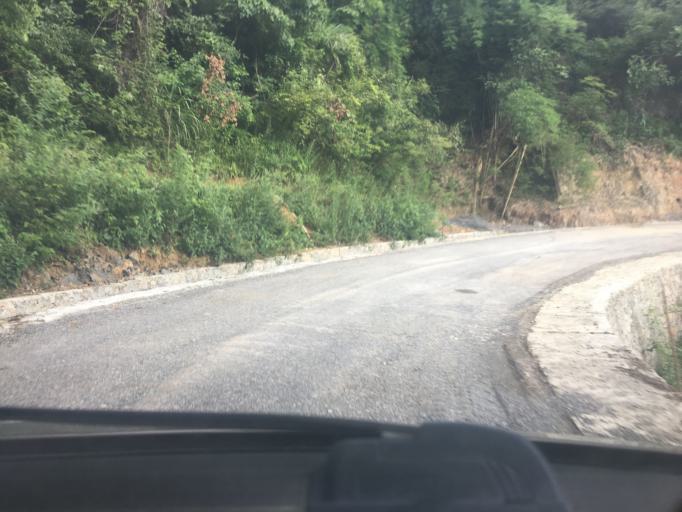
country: CN
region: Guizhou Sheng
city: Jiancha
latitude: 28.2010
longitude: 107.9911
